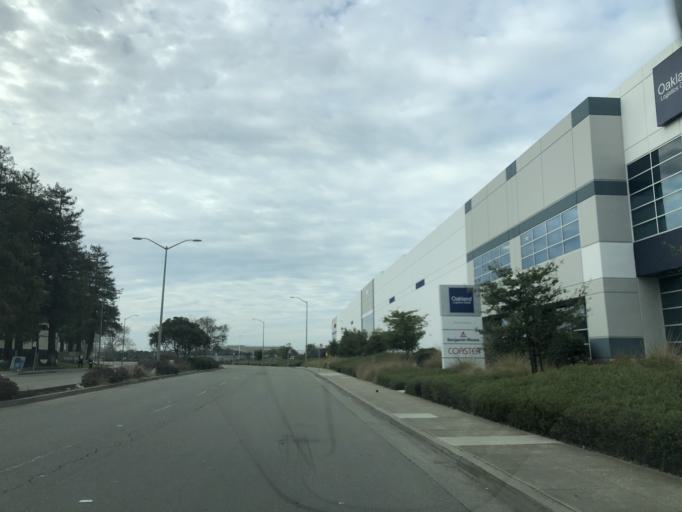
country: US
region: California
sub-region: Alameda County
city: Alameda
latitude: 37.7328
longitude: -122.2052
